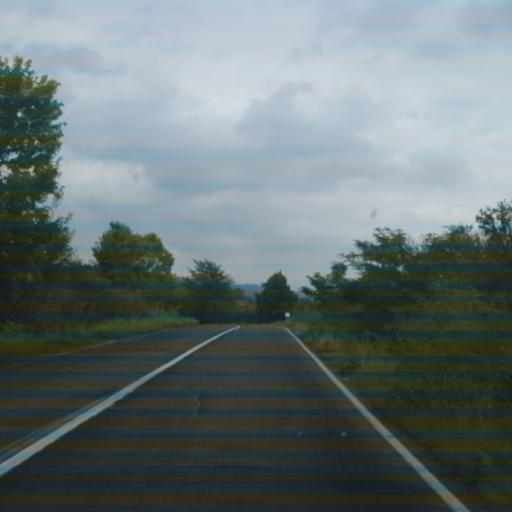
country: RS
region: Central Serbia
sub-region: Nisavski Okrug
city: Aleksinac
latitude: 43.5831
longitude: 21.6566
